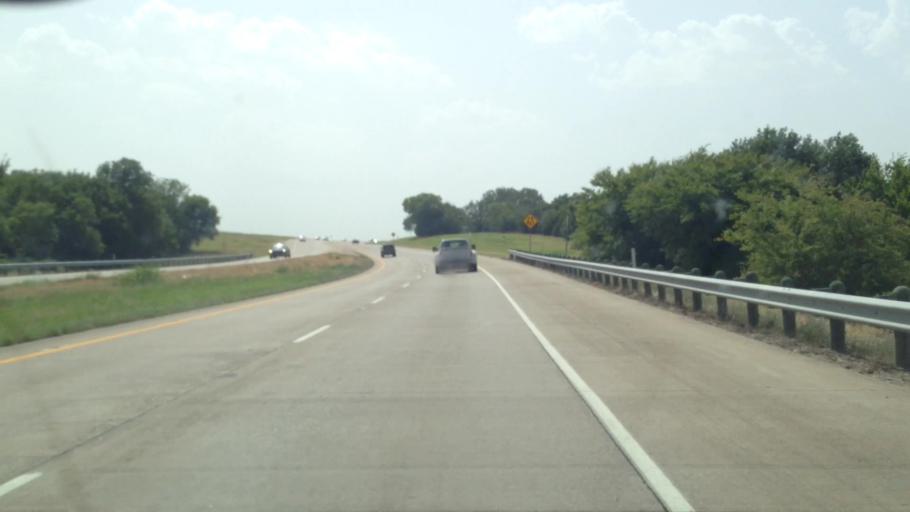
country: US
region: Texas
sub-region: Collin County
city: Princeton
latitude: 33.1637
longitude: -96.4375
